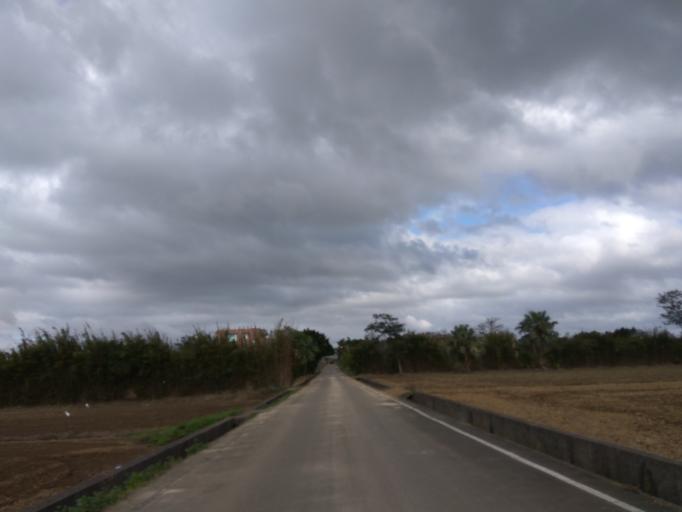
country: TW
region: Taiwan
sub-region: Hsinchu
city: Zhubei
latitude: 24.9690
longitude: 121.0902
